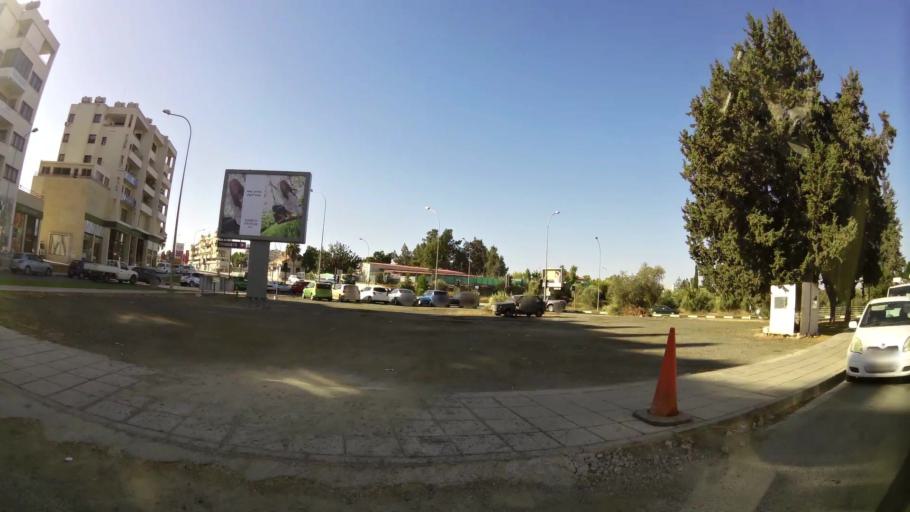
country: CY
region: Larnaka
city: Larnaca
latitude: 34.9269
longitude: 33.6155
